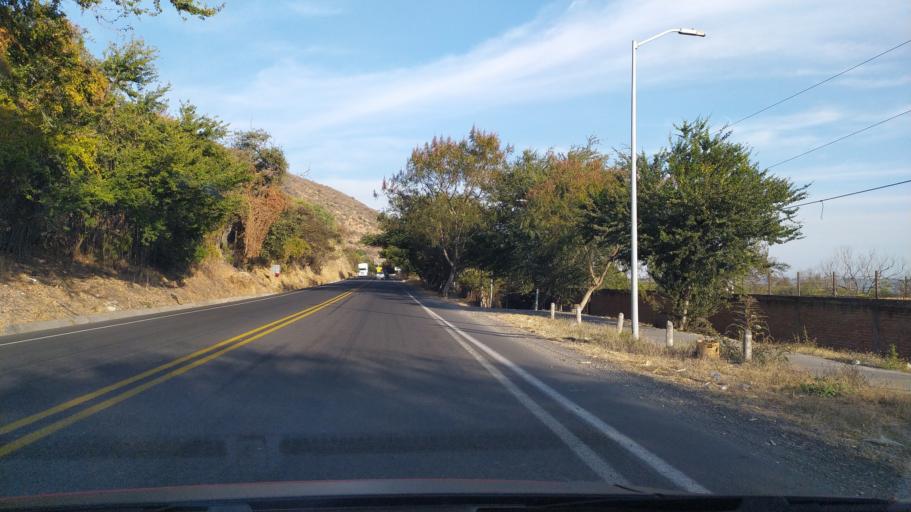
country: MX
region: Jalisco
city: Jamay
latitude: 20.2937
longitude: -102.7421
